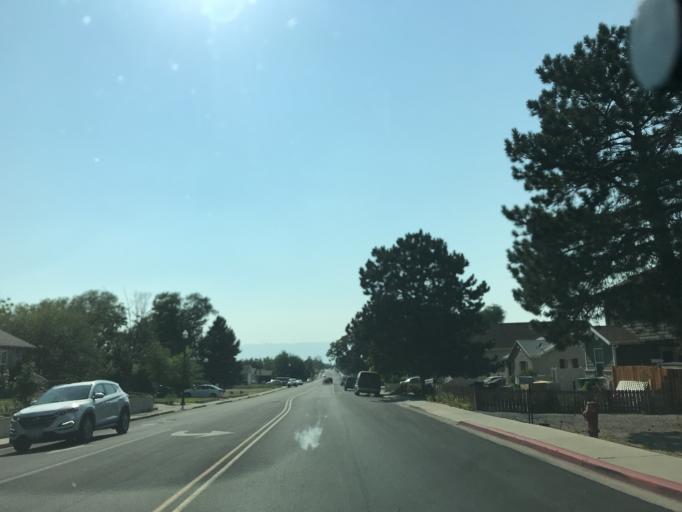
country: US
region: Utah
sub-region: Utah County
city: Orem
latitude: 40.2824
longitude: -111.6911
